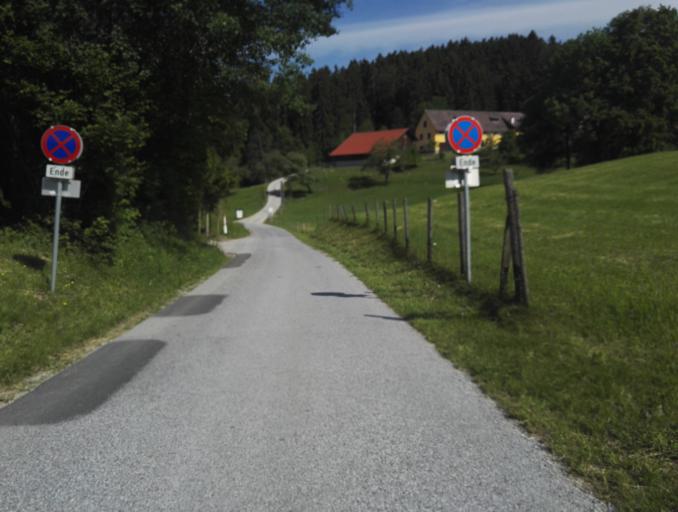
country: AT
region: Styria
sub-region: Politischer Bezirk Graz-Umgebung
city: Stattegg
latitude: 47.1621
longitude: 15.4288
